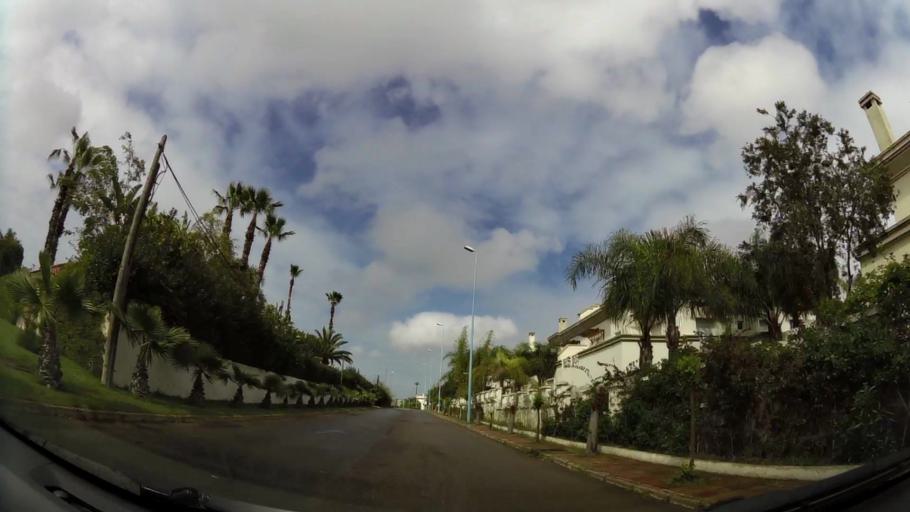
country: MA
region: Grand Casablanca
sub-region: Casablanca
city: Casablanca
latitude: 33.5285
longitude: -7.6204
